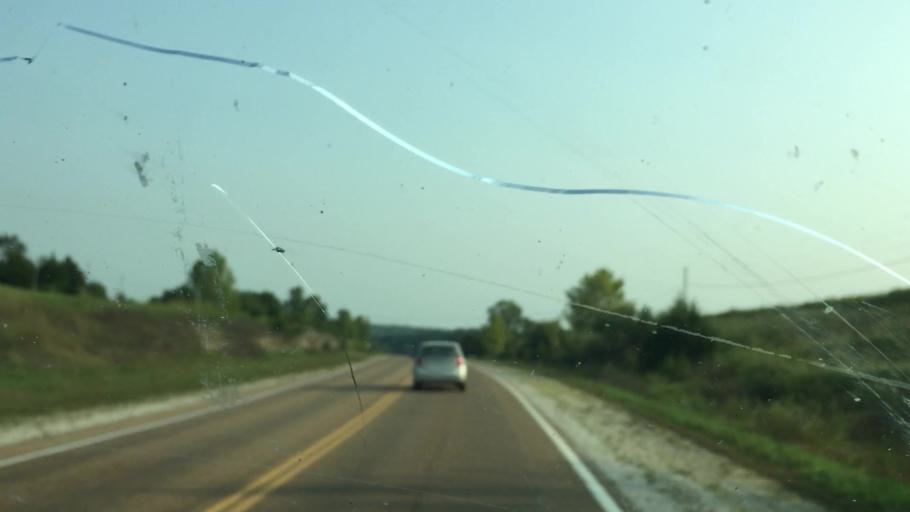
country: US
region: Missouri
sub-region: Pulaski County
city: Richland
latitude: 37.8107
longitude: -92.4068
